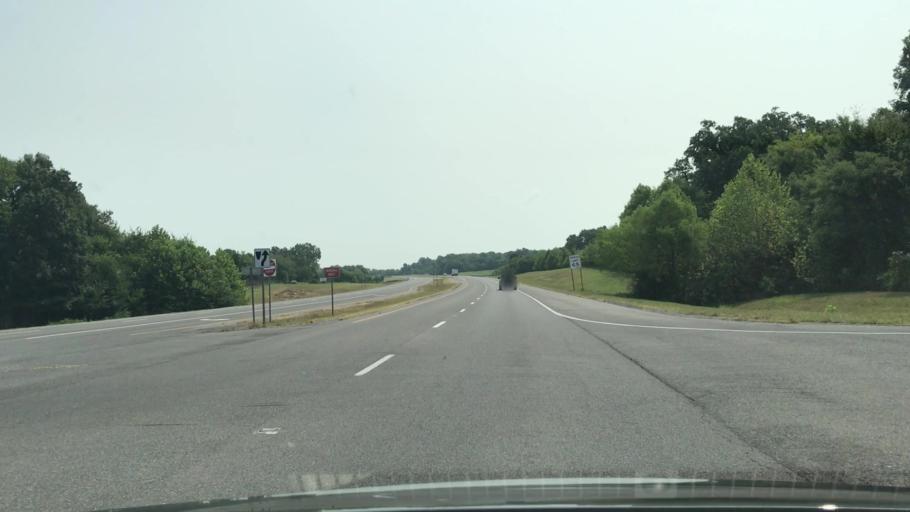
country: US
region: Kentucky
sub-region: Calloway County
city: Murray
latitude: 36.6491
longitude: -88.2498
